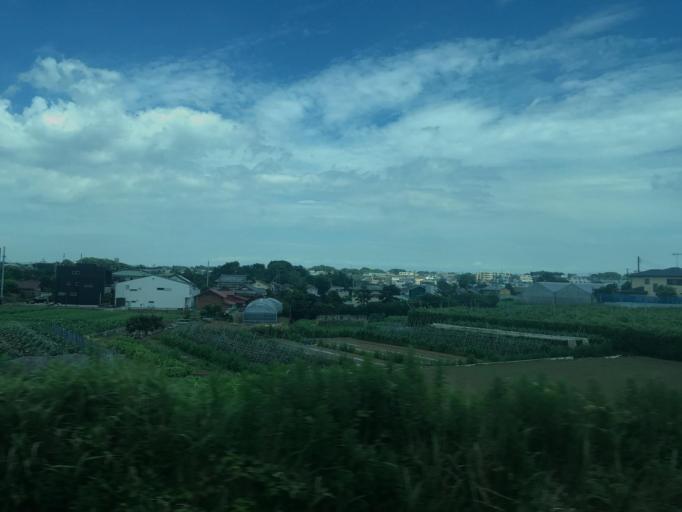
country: JP
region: Kanagawa
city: Fujisawa
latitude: 35.3719
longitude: 139.4729
